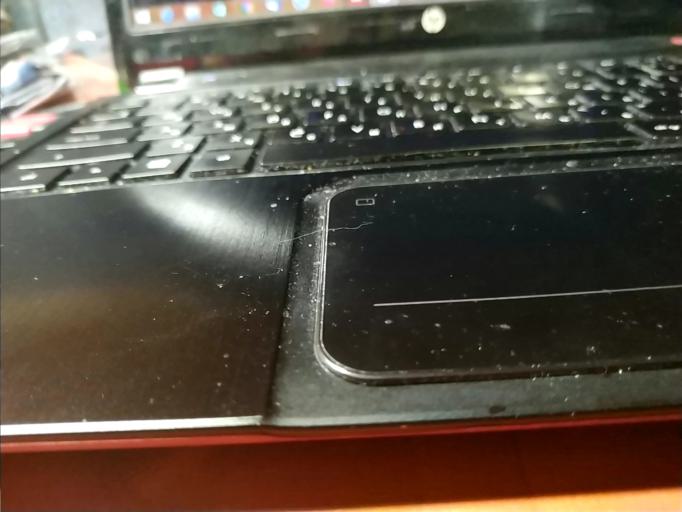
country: RU
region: Tverskaya
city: Ves'yegonsk
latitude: 58.7057
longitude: 37.5439
